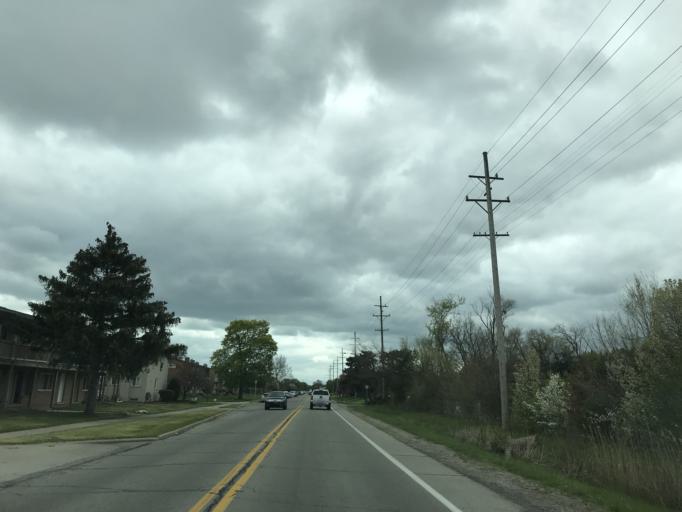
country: US
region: Michigan
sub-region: Wayne County
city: Riverview
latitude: 42.1894
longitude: -83.1798
